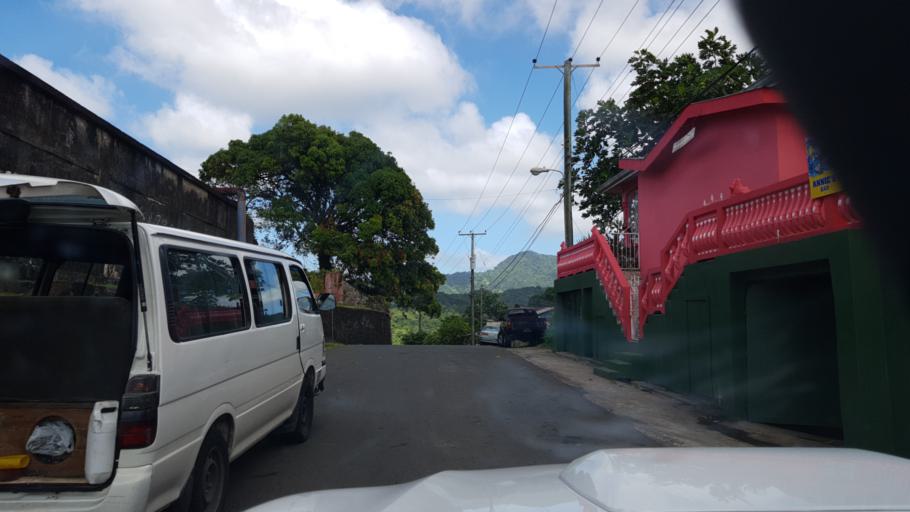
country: LC
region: Anse-la-Raye
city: Anse La Raye
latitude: 13.9407
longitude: -60.9804
